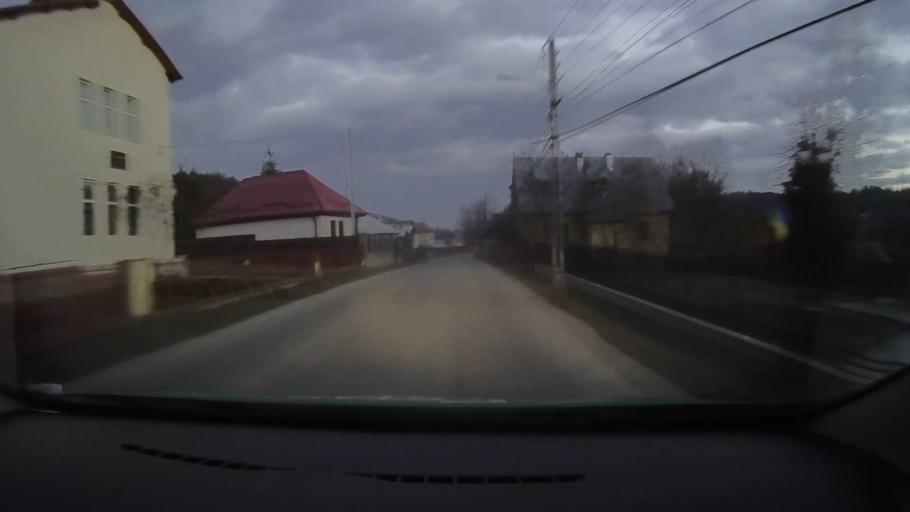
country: RO
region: Prahova
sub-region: Comuna Provita de Sus
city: Provita de Sus
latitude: 45.1353
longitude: 25.6387
